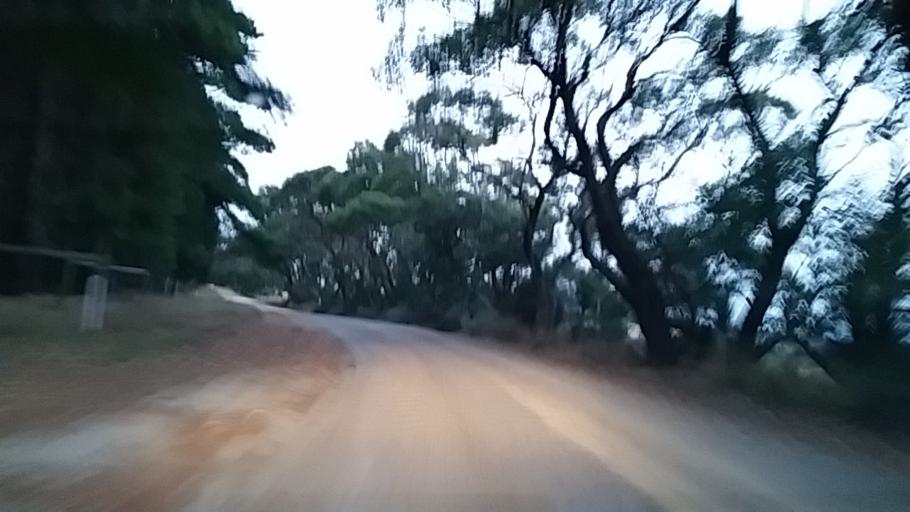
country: AU
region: South Australia
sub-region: Yankalilla
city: Normanville
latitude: -35.6101
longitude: 138.1783
